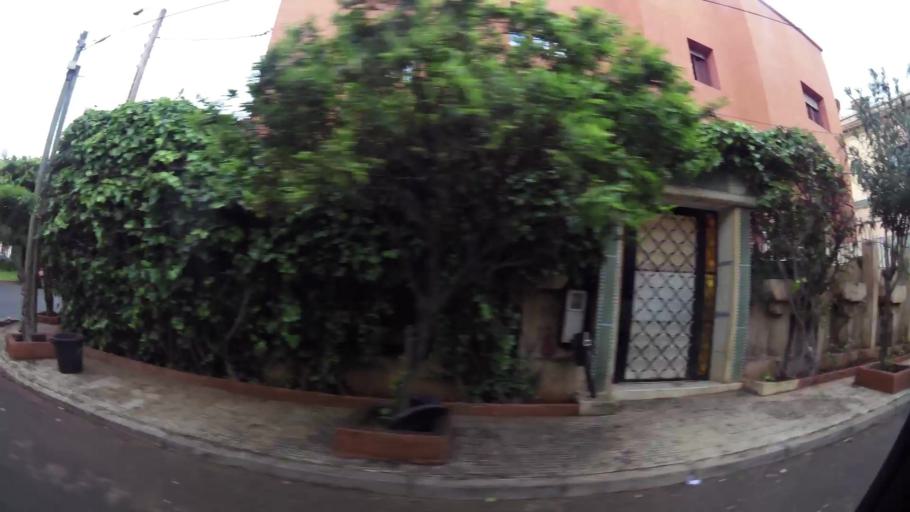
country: MA
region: Grand Casablanca
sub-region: Casablanca
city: Casablanca
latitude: 33.5631
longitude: -7.6766
